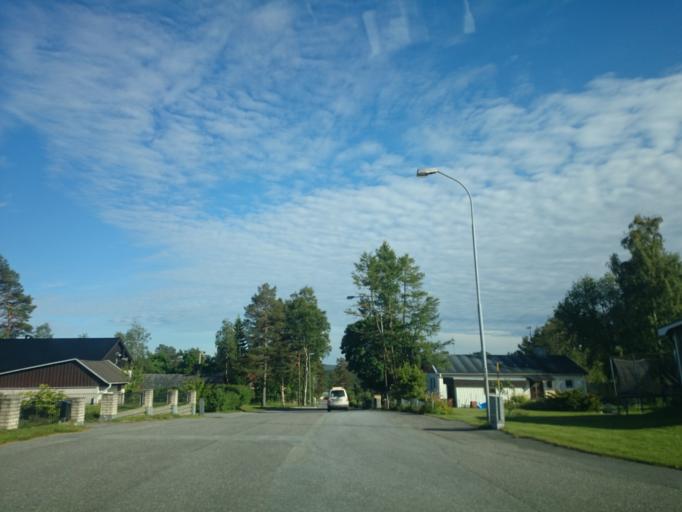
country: SE
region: Vaesternorrland
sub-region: Haernoesands Kommun
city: Haernoesand
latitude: 62.6486
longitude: 17.8920
